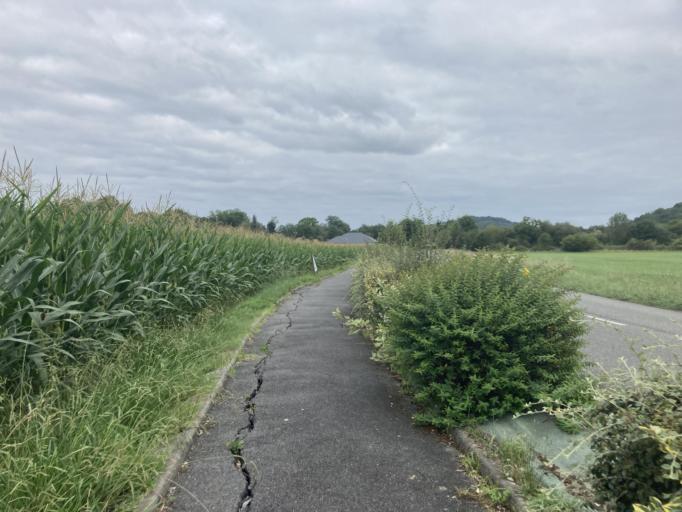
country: FR
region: Aquitaine
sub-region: Departement des Pyrenees-Atlantiques
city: Arbus
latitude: 43.3251
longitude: -0.4911
